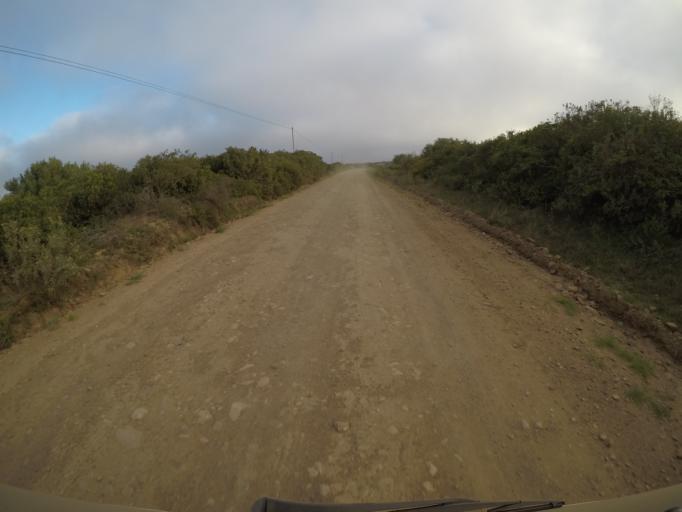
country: ZA
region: Western Cape
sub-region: Eden District Municipality
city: Mossel Bay
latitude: -34.1388
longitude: 22.0406
